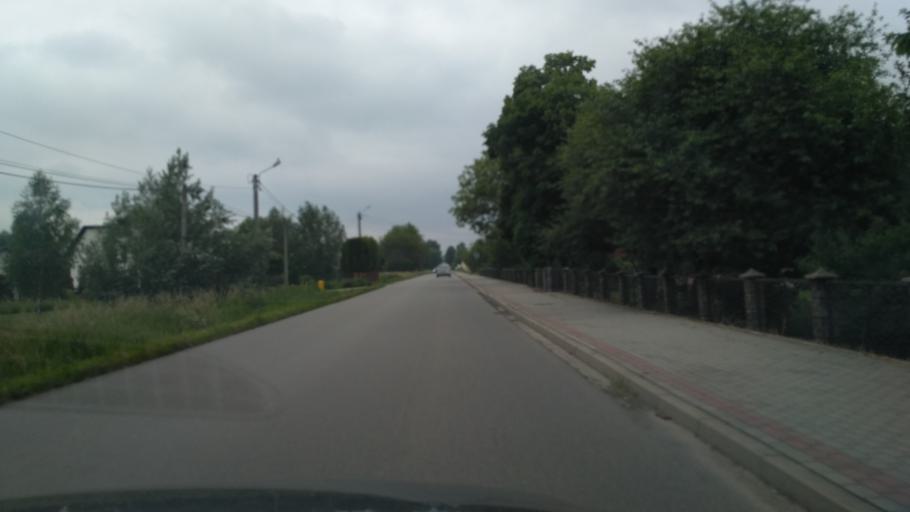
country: PL
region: Subcarpathian Voivodeship
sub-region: Powiat ropczycko-sedziszowski
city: Sedziszow Malopolski
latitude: 50.0825
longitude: 21.6709
